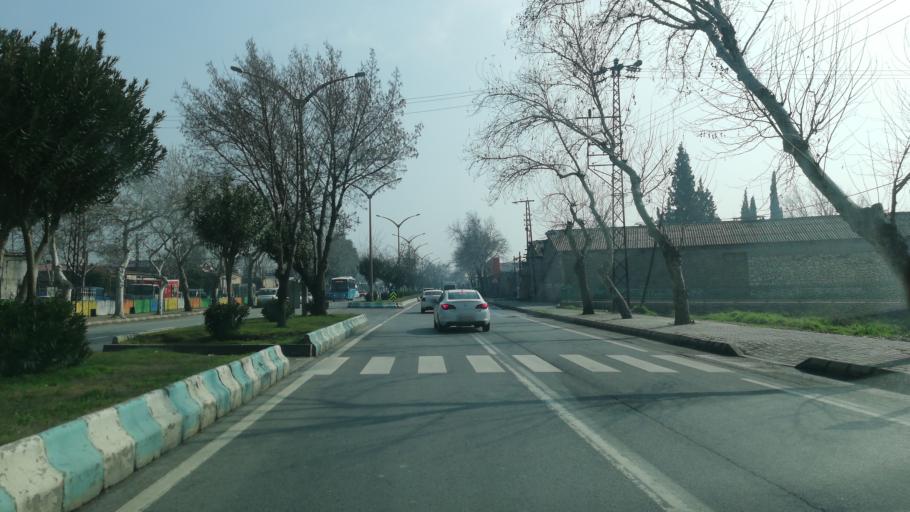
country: TR
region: Kahramanmaras
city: Kahramanmaras
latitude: 37.5634
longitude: 36.9528
